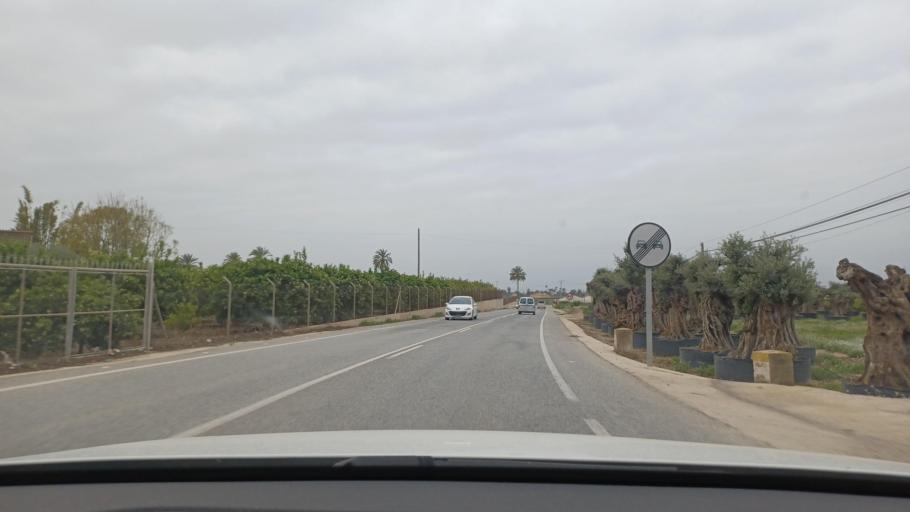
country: ES
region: Valencia
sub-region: Provincia de Alicante
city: Elche
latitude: 38.2389
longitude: -0.7114
